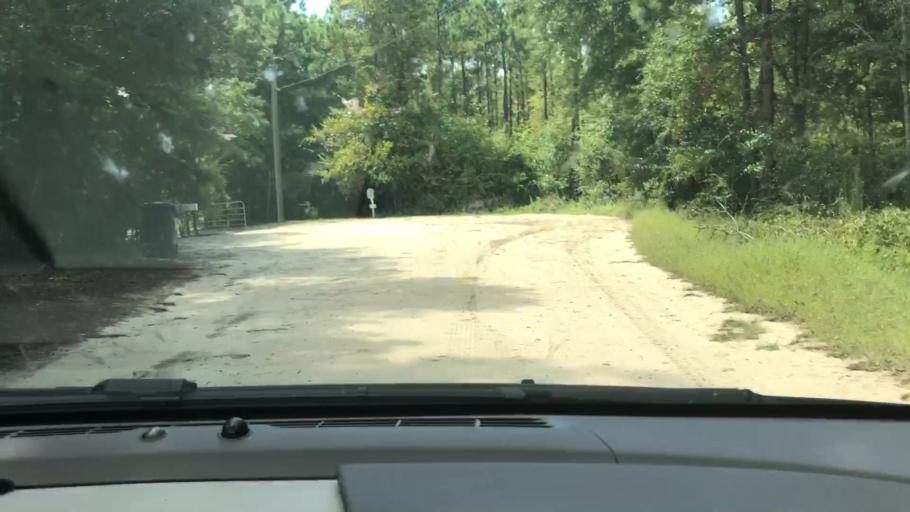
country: US
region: Georgia
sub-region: Clay County
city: Fort Gaines
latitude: 31.7311
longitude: -85.0901
